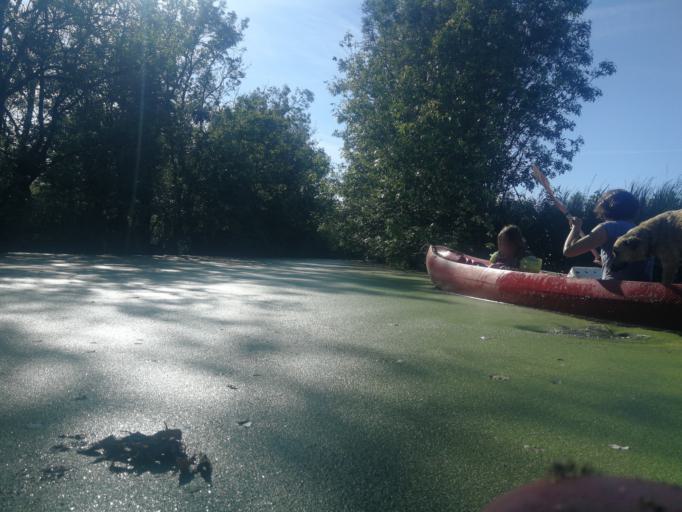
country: FR
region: Poitou-Charentes
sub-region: Departement de la Charente-Maritime
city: Marans
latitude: 46.3606
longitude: -0.9531
